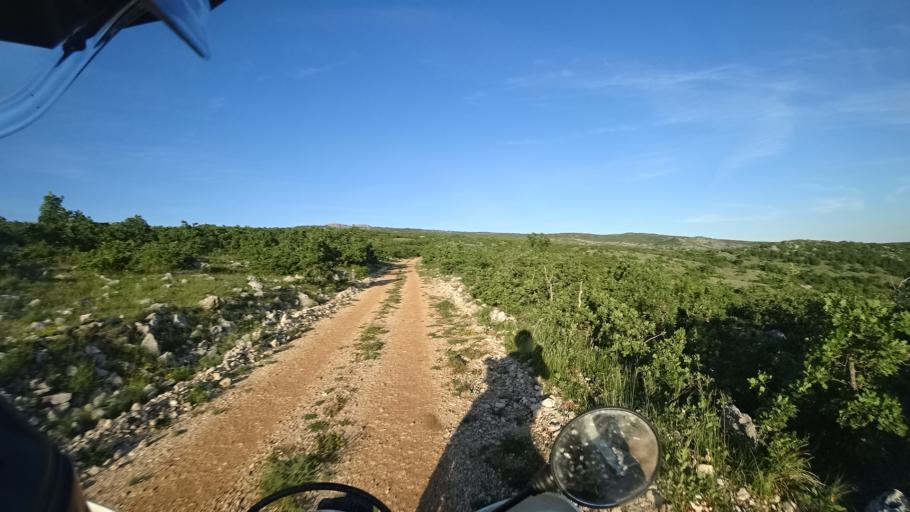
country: HR
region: Sibensko-Kniniska
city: Drnis
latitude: 43.8497
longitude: 16.3444
